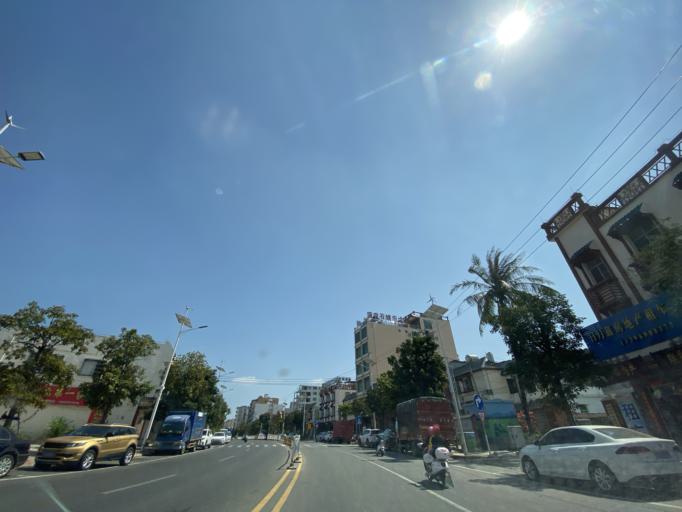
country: CN
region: Hainan
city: Yingzhou
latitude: 18.4221
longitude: 109.8475
